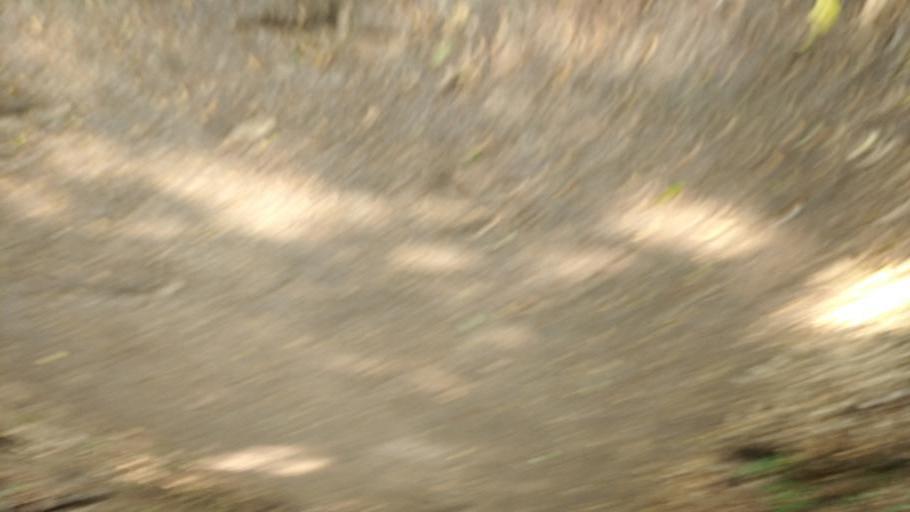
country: HU
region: Pest
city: Nagymaros
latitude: 47.7867
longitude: 18.9340
